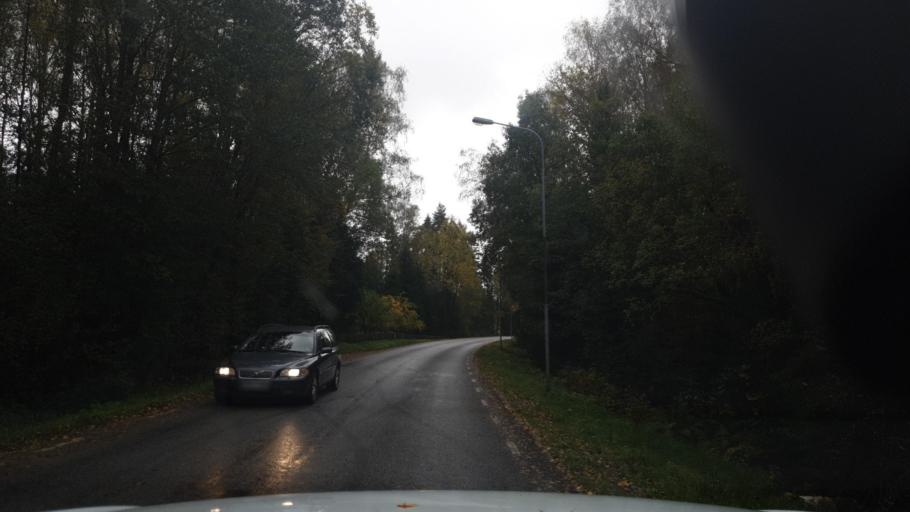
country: SE
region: Vaermland
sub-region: Karlstads Kommun
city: Valberg
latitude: 59.4106
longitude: 13.1780
